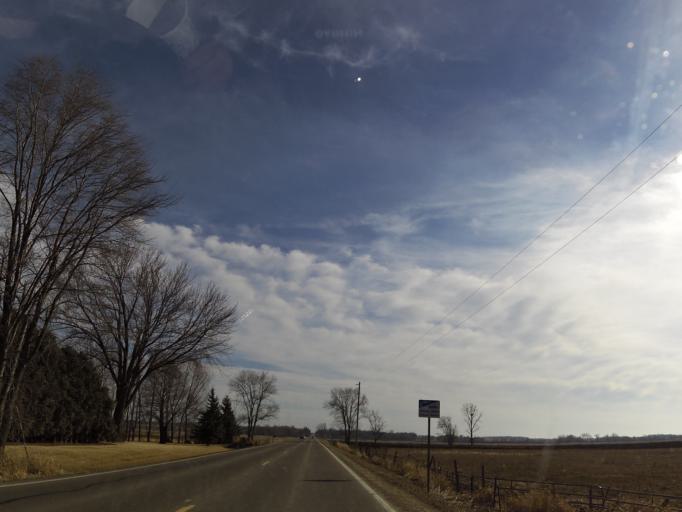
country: US
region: Minnesota
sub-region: Rice County
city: Northfield
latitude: 44.5040
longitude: -93.2006
